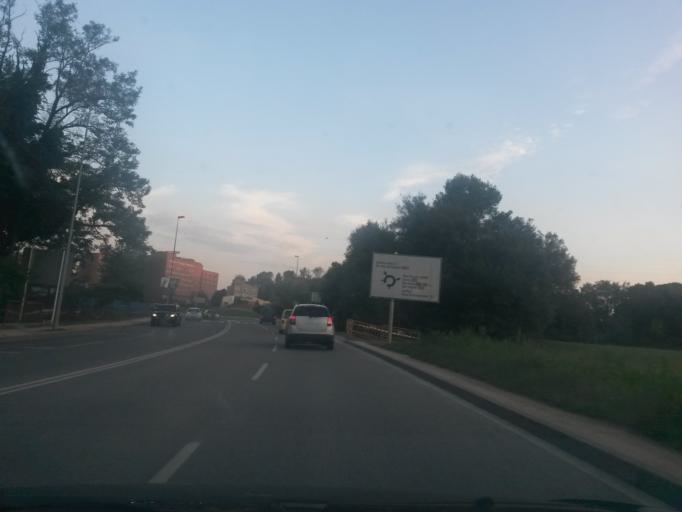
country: ES
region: Catalonia
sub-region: Provincia de Girona
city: Girona
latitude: 42.0008
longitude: 2.8165
